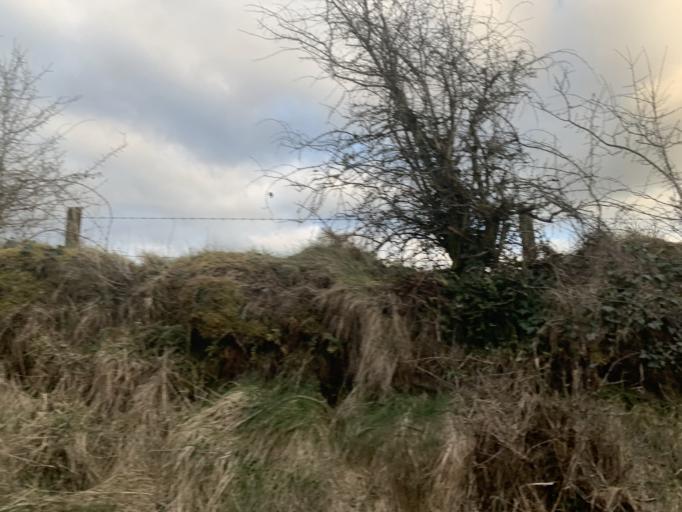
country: IE
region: Connaught
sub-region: Maigh Eo
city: Ballyhaunis
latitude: 53.8414
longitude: -8.7225
